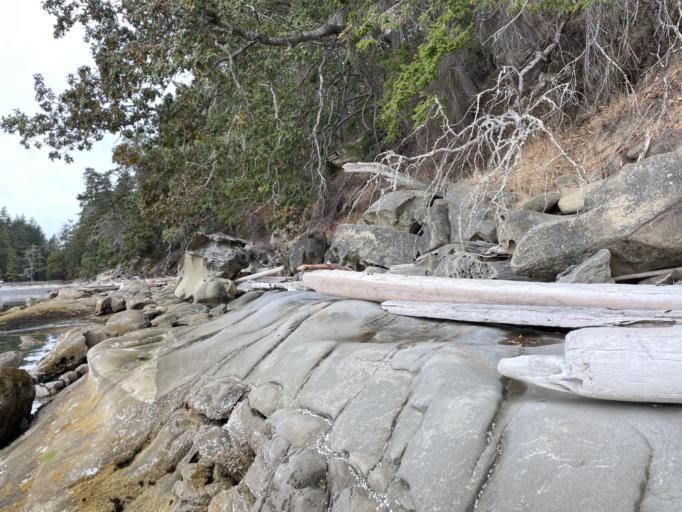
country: CA
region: British Columbia
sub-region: Cowichan Valley Regional District
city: Ladysmith
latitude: 49.0930
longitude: -123.7228
